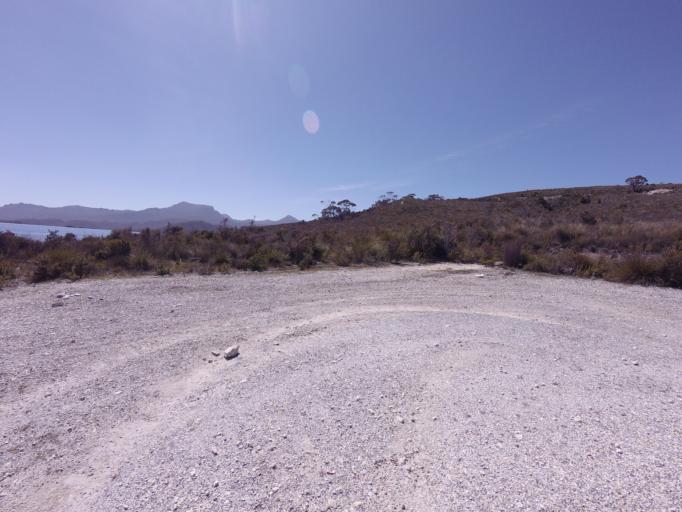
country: AU
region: Tasmania
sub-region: Huon Valley
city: Geeveston
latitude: -43.0319
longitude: 146.3331
